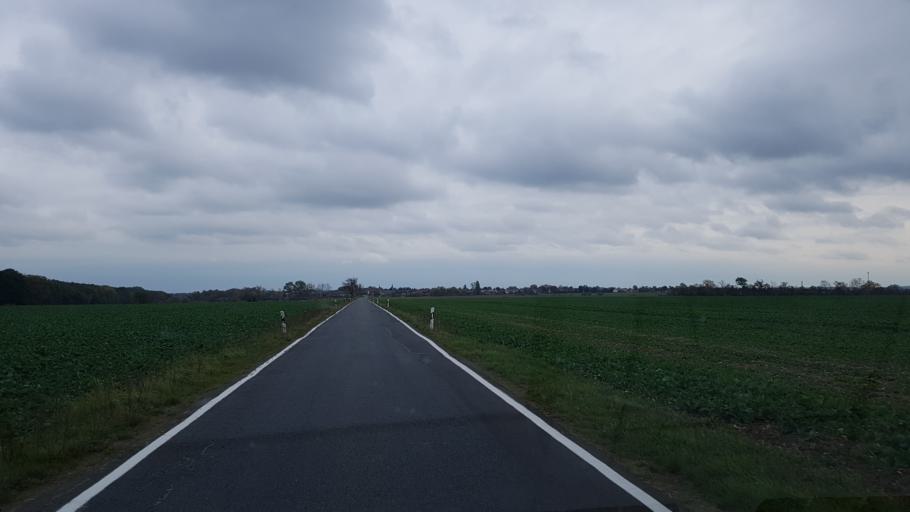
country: DE
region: Saxony
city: Dahlen
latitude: 51.3727
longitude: 12.9712
